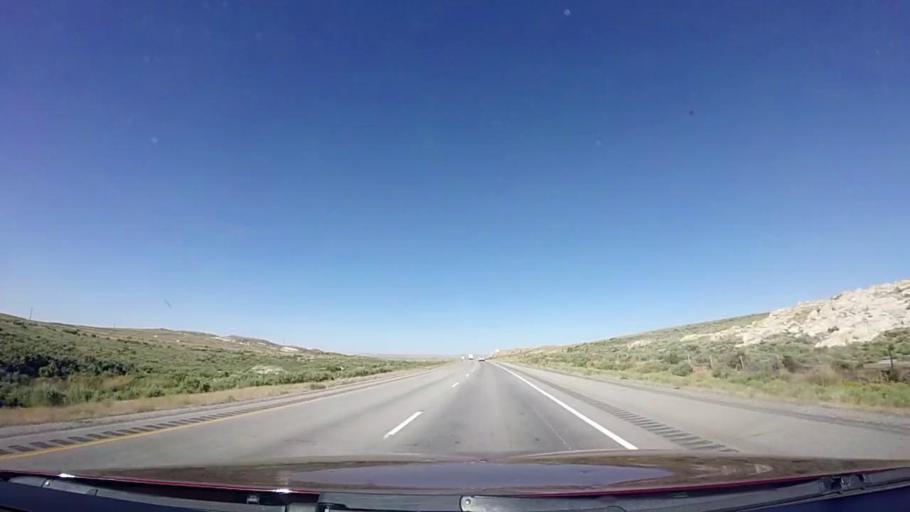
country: US
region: Wyoming
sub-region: Carbon County
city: Rawlins
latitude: 41.7889
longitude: -107.3926
